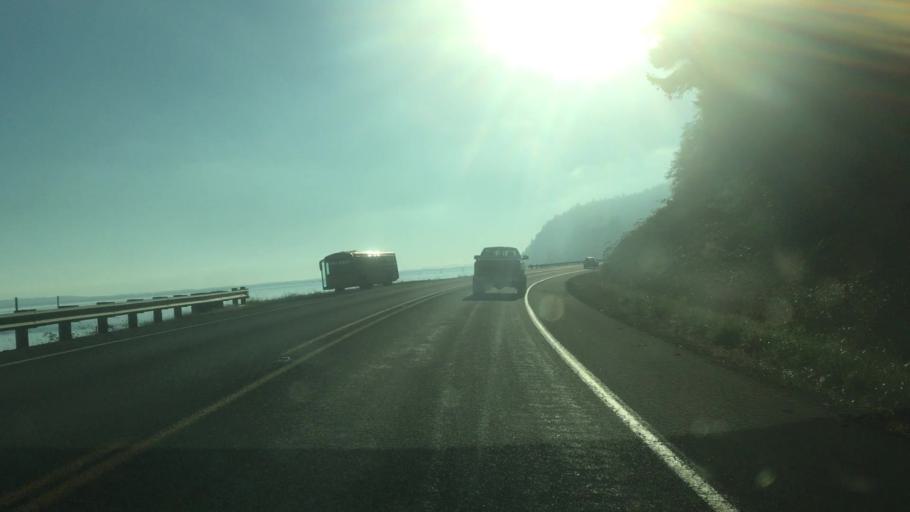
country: US
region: Oregon
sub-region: Clatsop County
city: Astoria
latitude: 46.2631
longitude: -123.8393
